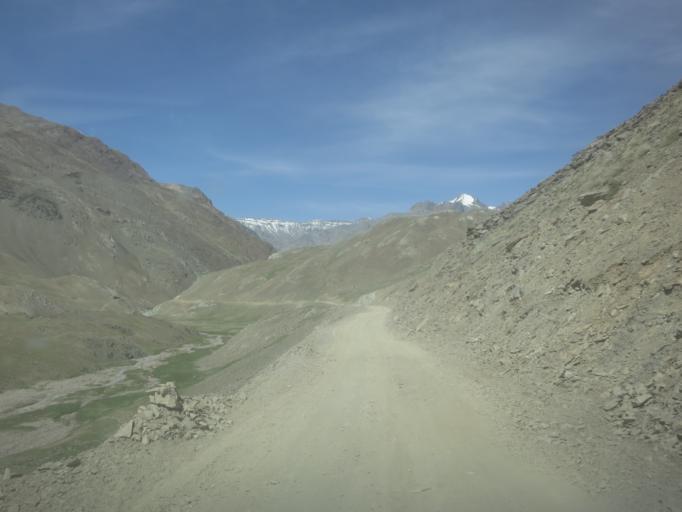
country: IN
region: Himachal Pradesh
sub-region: Kulu
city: Manali
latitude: 32.4130
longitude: 77.6459
